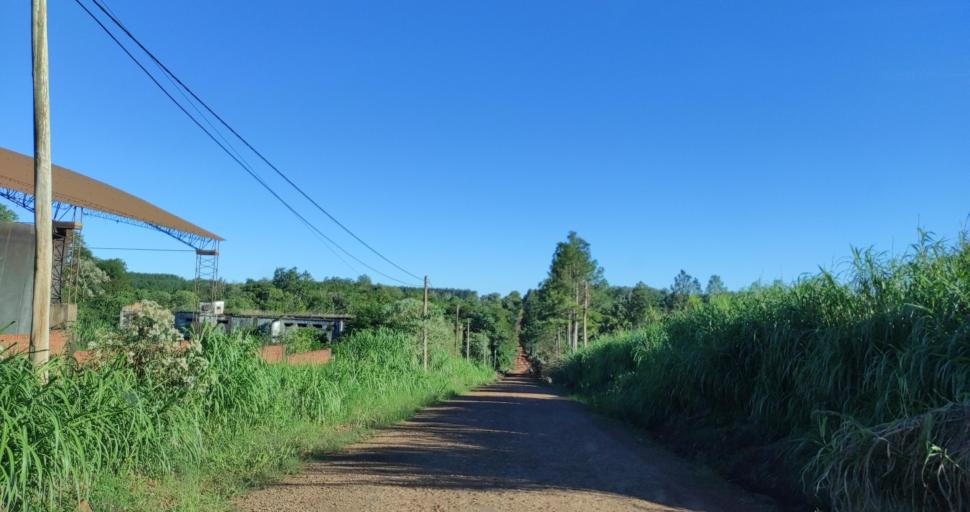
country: AR
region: Misiones
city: Puerto Rico
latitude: -26.8256
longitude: -55.0112
